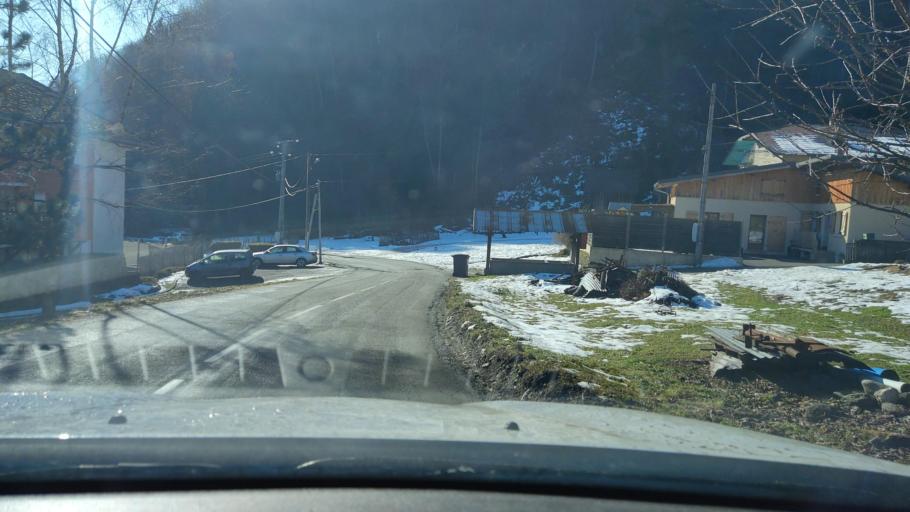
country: FR
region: Rhone-Alpes
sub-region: Departement de la Savoie
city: La Bathie
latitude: 45.5959
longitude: 6.4391
